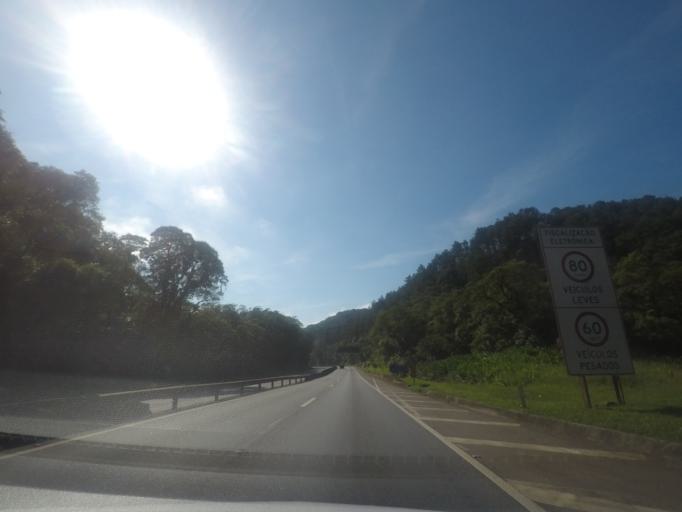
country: BR
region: Parana
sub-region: Piraquara
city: Piraquara
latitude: -25.5968
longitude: -48.9016
